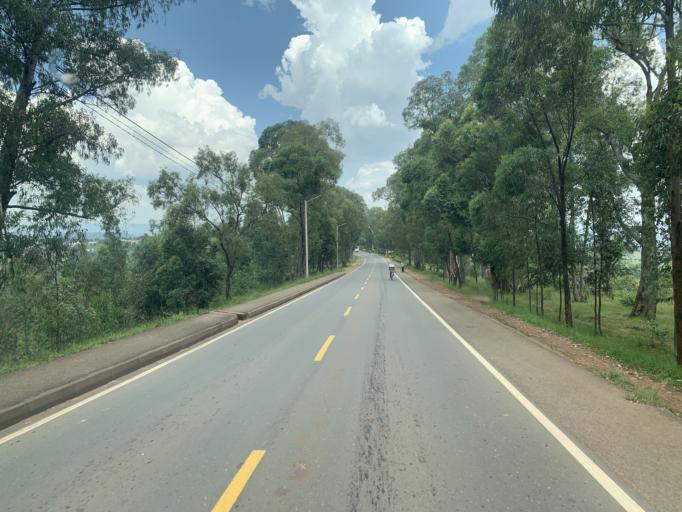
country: RW
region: Kigali
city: Kigali
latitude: -1.9989
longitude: 29.9068
